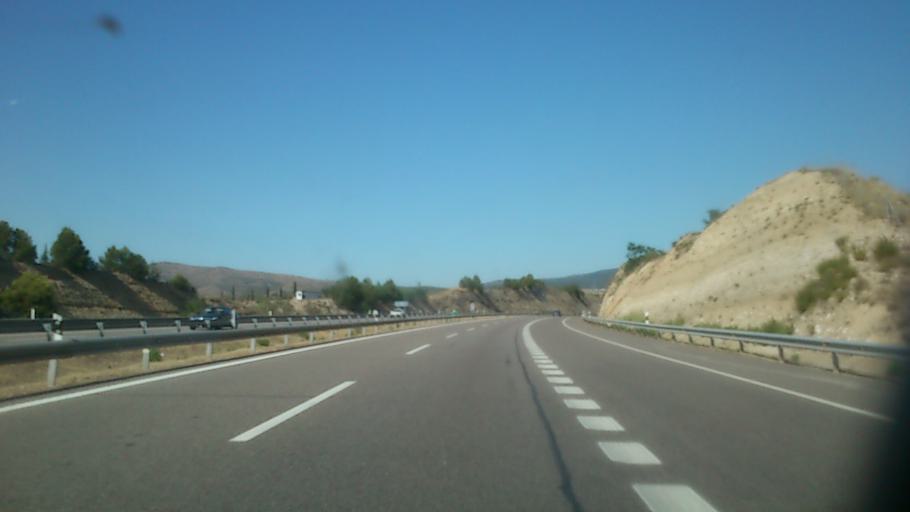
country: ES
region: Aragon
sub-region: Provincia de Zaragoza
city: Calatayud
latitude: 41.3562
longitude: -1.6130
